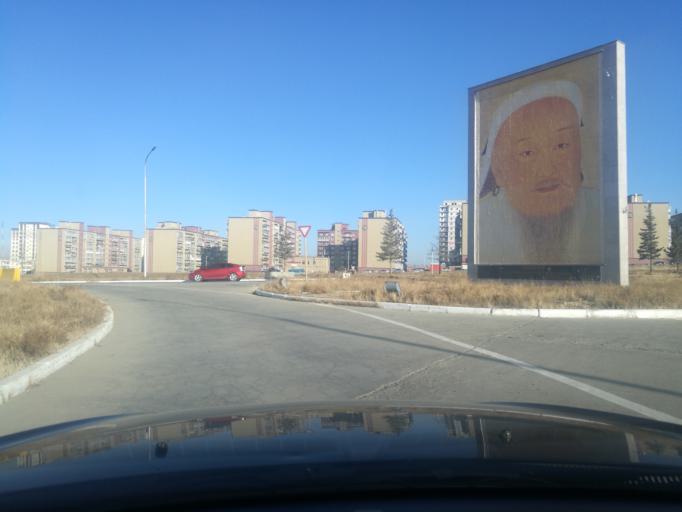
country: MN
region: Ulaanbaatar
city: Ulaanbaatar
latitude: 47.8541
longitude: 106.7652
